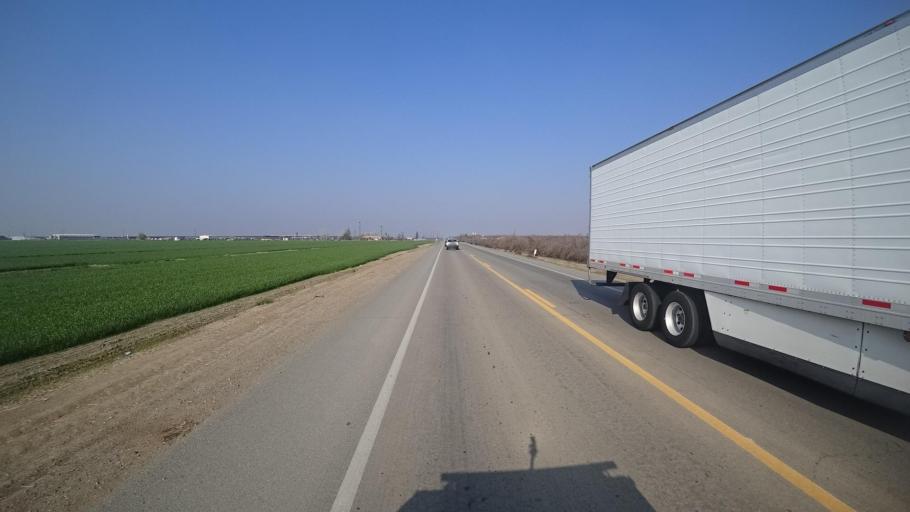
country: US
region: California
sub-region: Kern County
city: Greenfield
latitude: 35.2422
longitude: -119.1099
